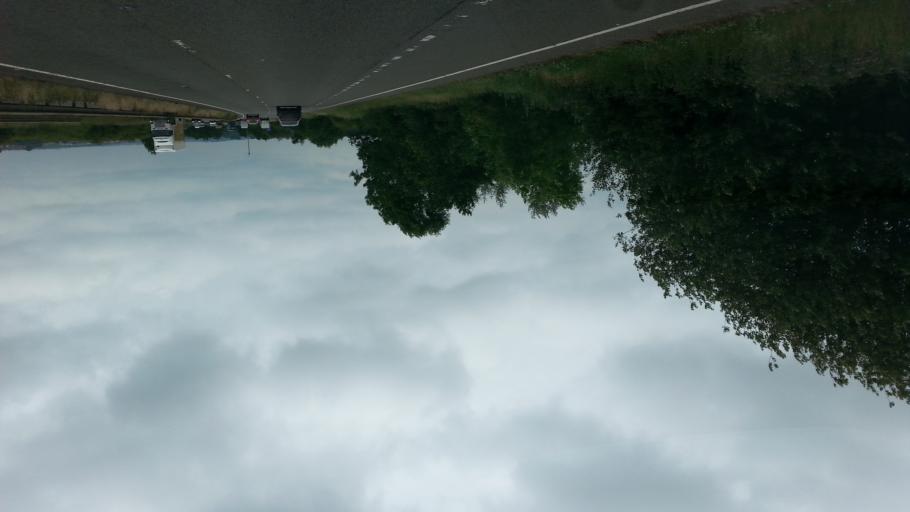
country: GB
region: England
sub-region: Leicestershire
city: Donisthorpe
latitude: 52.6942
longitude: -1.5468
